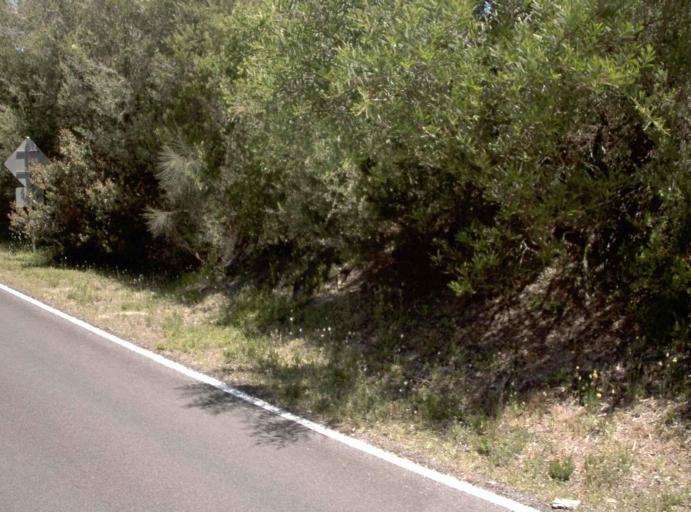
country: AU
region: Victoria
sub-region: Latrobe
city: Morwell
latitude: -38.8748
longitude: 146.2671
